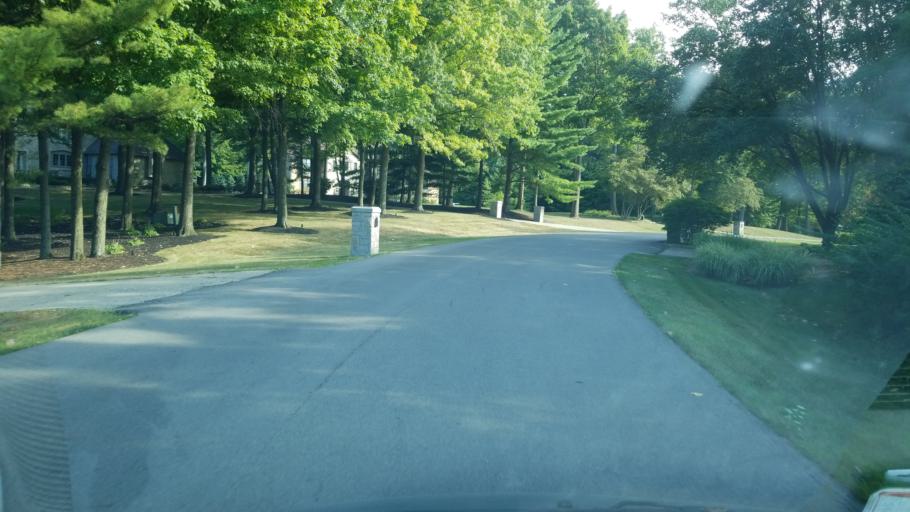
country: US
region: Ohio
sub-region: Delaware County
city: Powell
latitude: 40.1440
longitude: -83.0516
